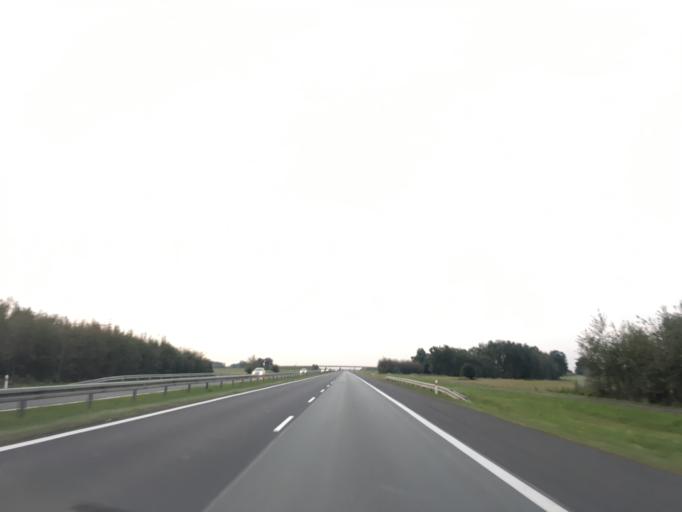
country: PL
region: Lodz Voivodeship
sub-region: Powiat piotrkowski
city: Grabica
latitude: 51.4906
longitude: 19.6139
